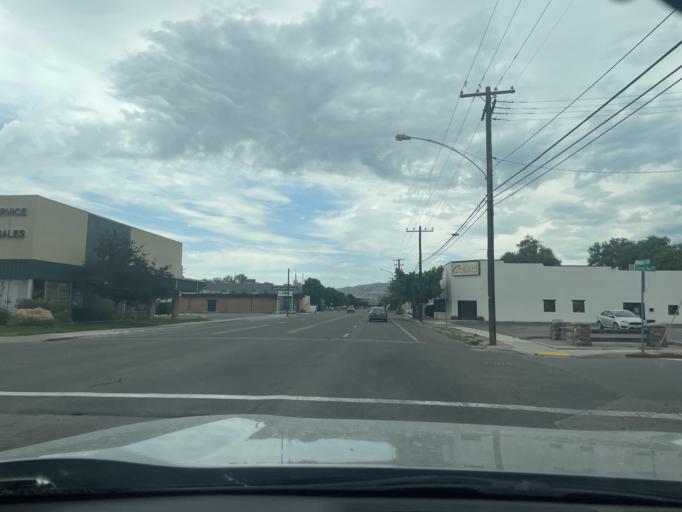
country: US
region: Utah
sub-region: Salt Lake County
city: South Salt Lake
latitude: 40.7096
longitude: -111.8911
